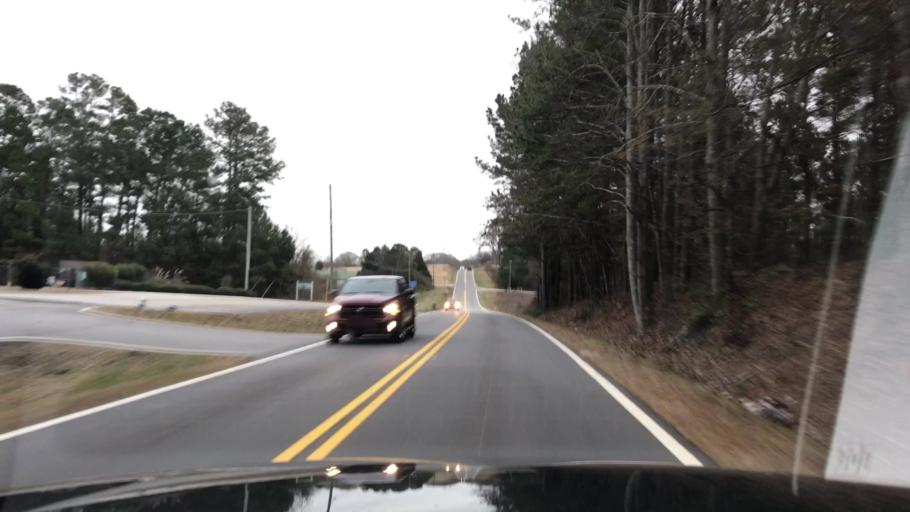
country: US
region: Georgia
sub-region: Walton County
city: Monroe
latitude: 33.8884
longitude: -83.7801
